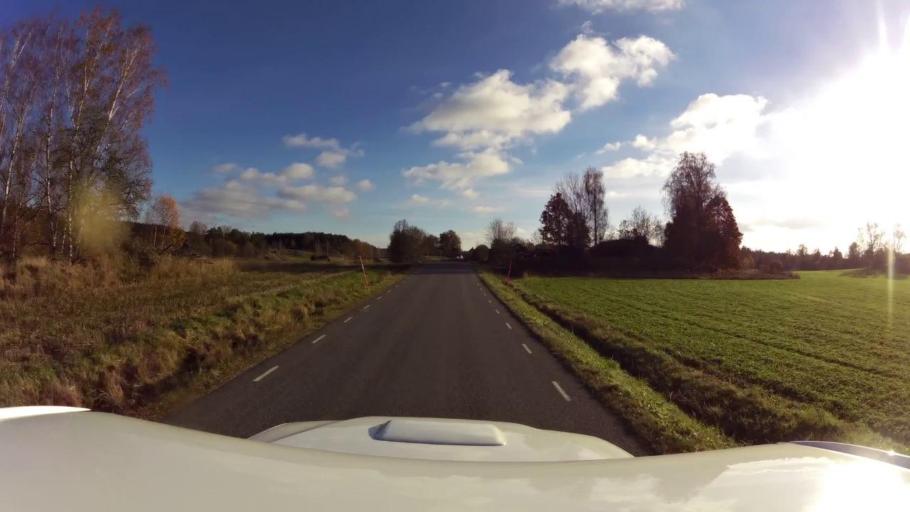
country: SE
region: OEstergoetland
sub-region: Linkopings Kommun
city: Vikingstad
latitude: 58.2583
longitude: 15.4603
